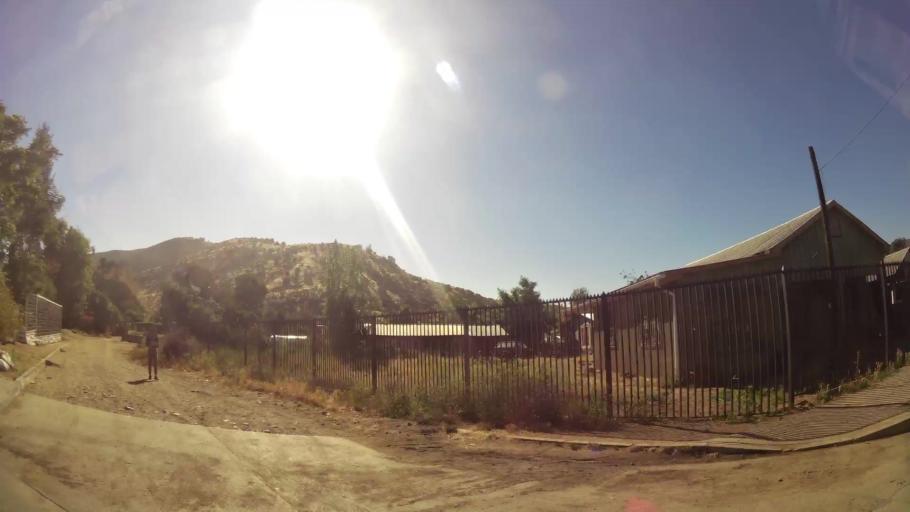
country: CL
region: Santiago Metropolitan
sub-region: Provincia de Chacabuco
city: Lampa
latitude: -33.3960
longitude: -71.1242
